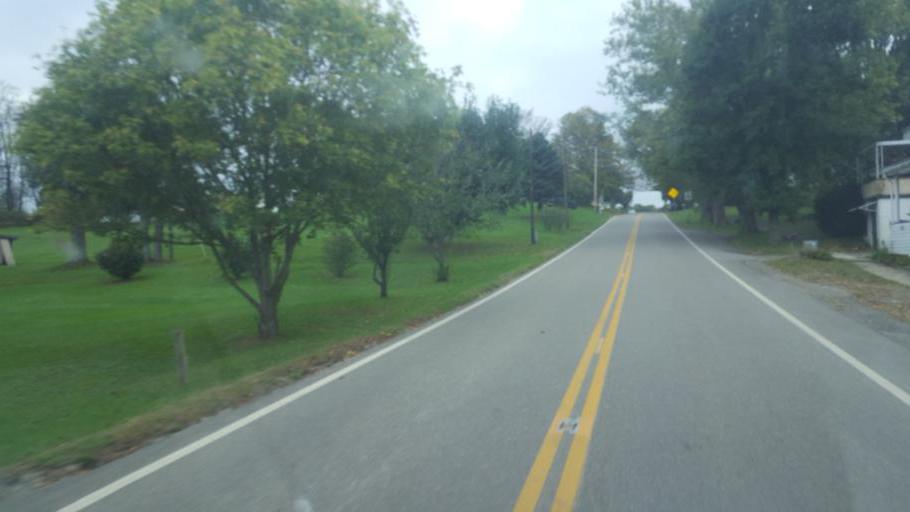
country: US
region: Ohio
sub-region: Harrison County
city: Cadiz
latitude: 40.4020
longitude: -81.0315
